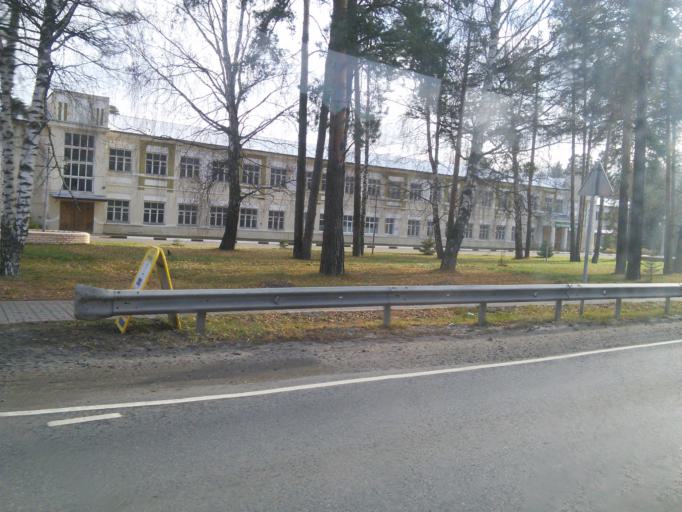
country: RU
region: Moskovskaya
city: Likino-Dulevo
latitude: 55.7149
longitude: 38.9583
